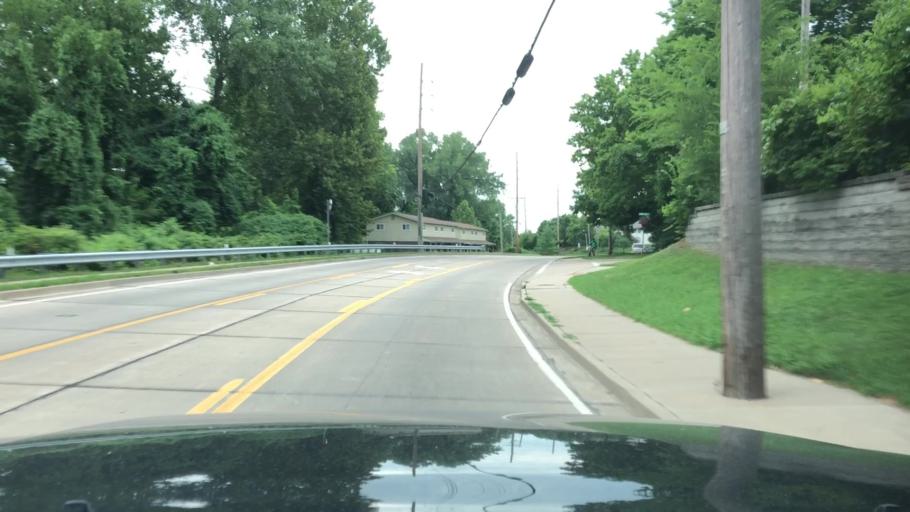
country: US
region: Missouri
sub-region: Saint Charles County
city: Saint Charles
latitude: 38.8126
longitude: -90.5127
